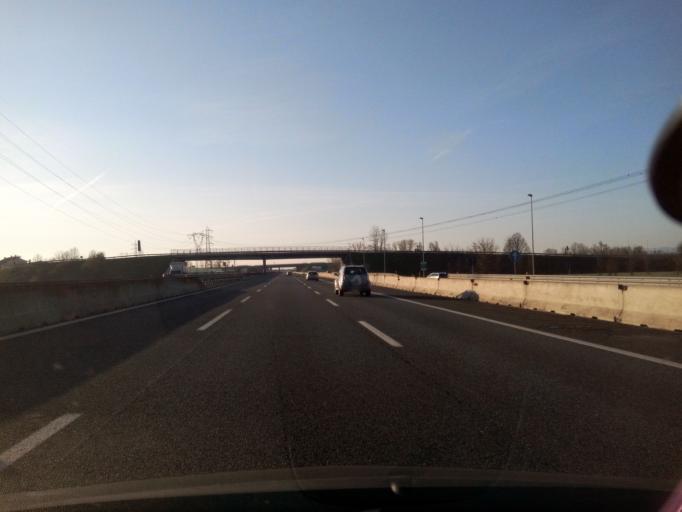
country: IT
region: Emilia-Romagna
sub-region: Provincia di Piacenza
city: Piacenza
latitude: 45.0564
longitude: 9.7433
